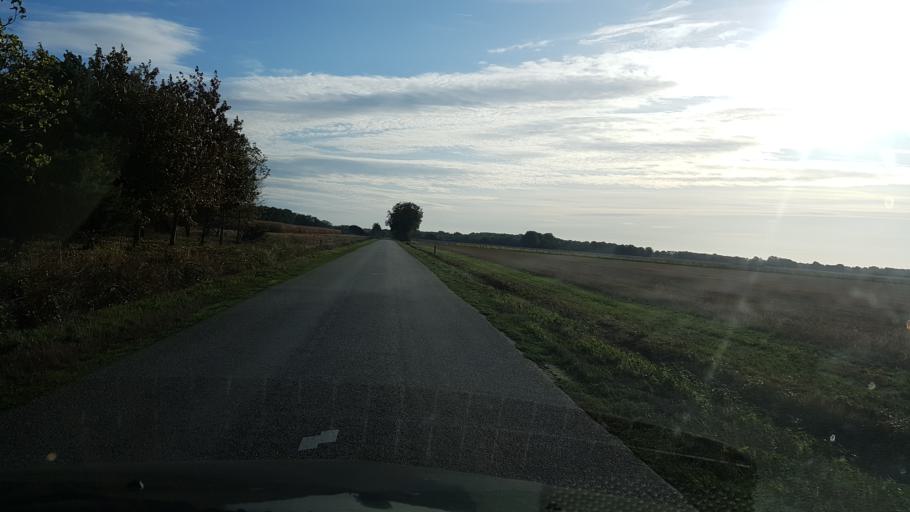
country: FR
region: Centre
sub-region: Departement du Loiret
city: Cerdon
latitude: 47.6711
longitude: 2.2912
